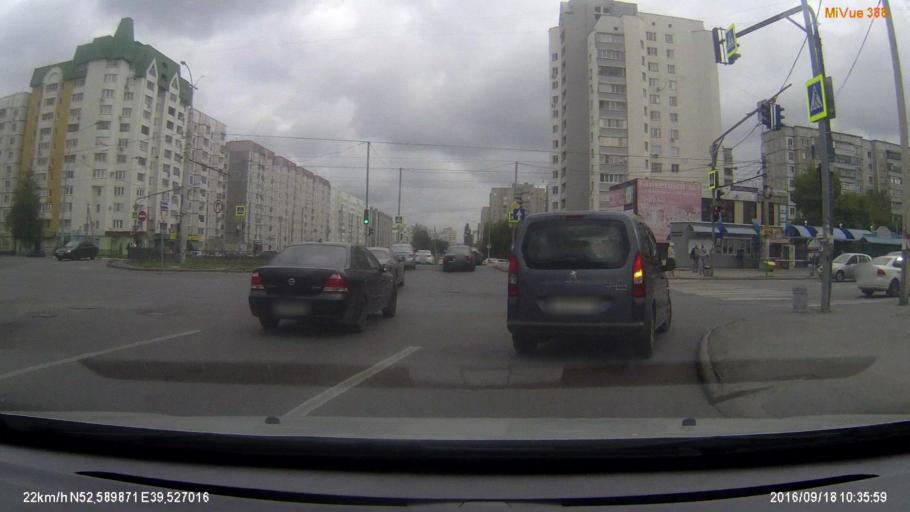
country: RU
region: Lipetsk
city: Syrskoye
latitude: 52.5841
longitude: 39.5303
